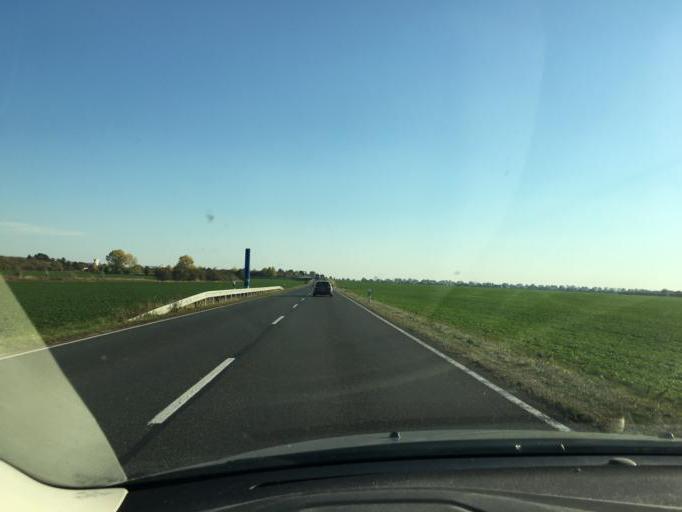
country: DE
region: Saxony
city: Rackwitz
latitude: 51.4285
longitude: 12.3715
